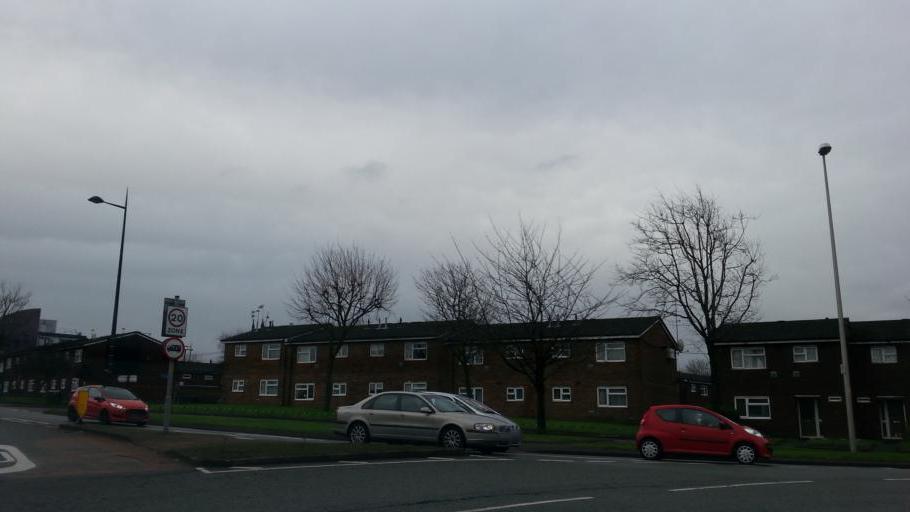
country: GB
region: England
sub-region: Sandwell
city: Oldbury
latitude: 52.5020
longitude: -2.0177
